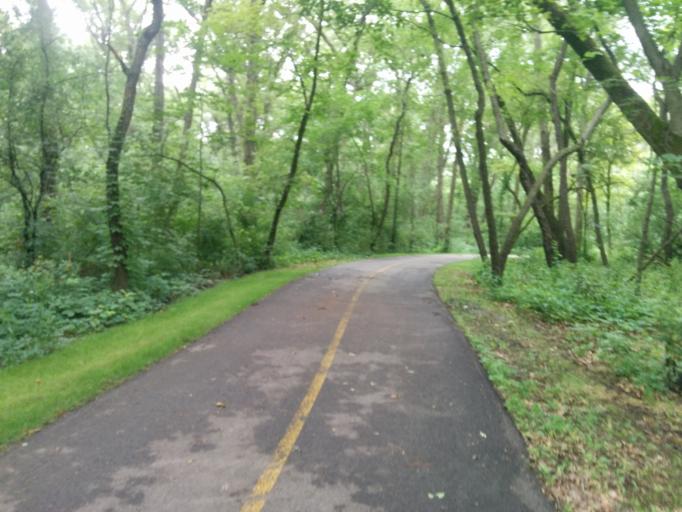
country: US
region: Illinois
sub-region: Cook County
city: Western Springs
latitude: 41.8242
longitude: -87.9025
